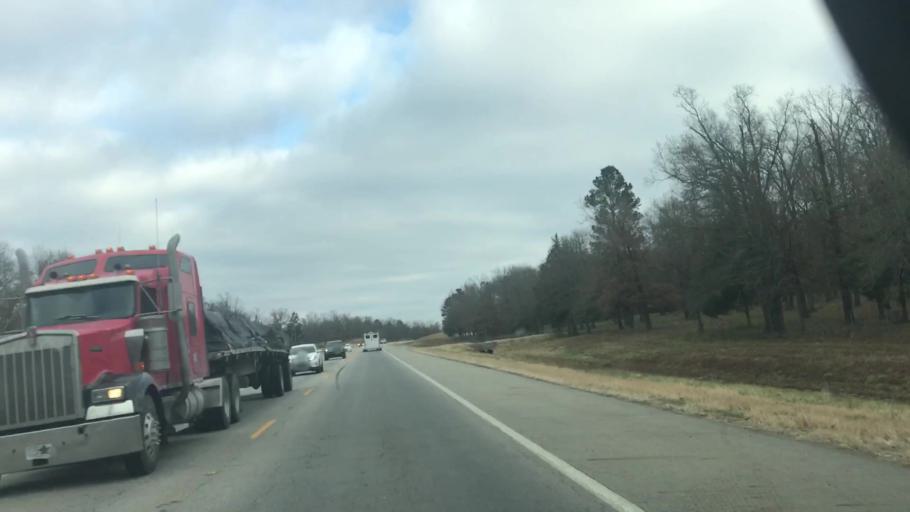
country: US
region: Arkansas
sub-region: Scott County
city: Waldron
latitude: 34.9184
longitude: -94.1071
